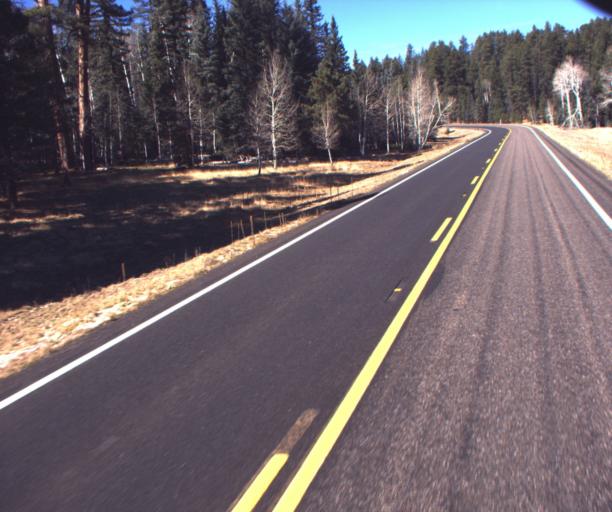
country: US
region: Arizona
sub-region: Coconino County
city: Grand Canyon
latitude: 36.5324
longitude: -112.1515
